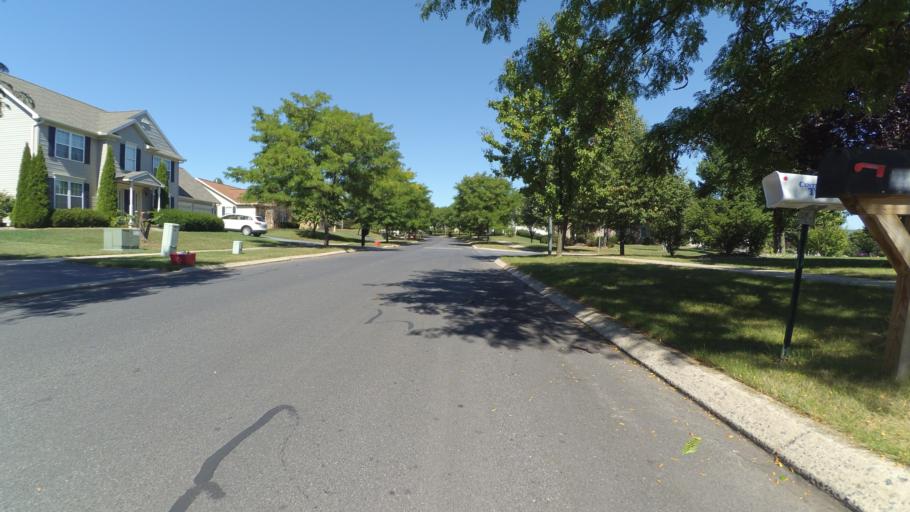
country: US
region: Pennsylvania
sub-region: Centre County
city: Pine Grove Mills
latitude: 40.7655
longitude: -77.8903
